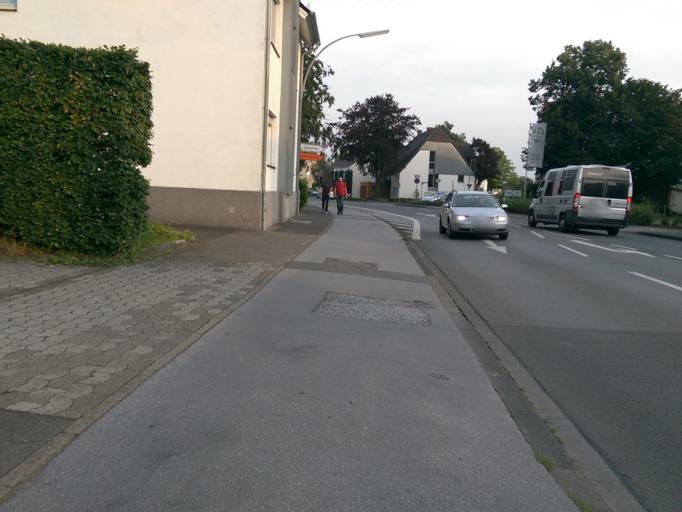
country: DE
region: North Rhine-Westphalia
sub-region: Regierungsbezirk Detmold
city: Rheda-Wiedenbruck
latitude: 51.8817
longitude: 8.2356
